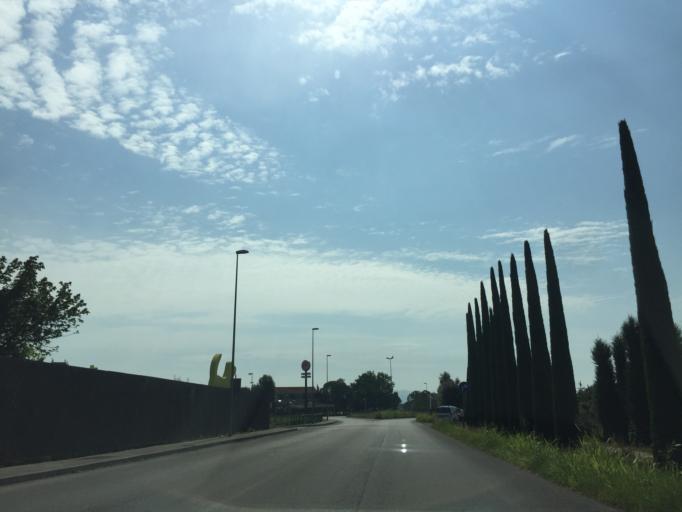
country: IT
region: Tuscany
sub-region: Provincia di Pistoia
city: Ponte Buggianese
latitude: 43.8593
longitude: 10.7607
